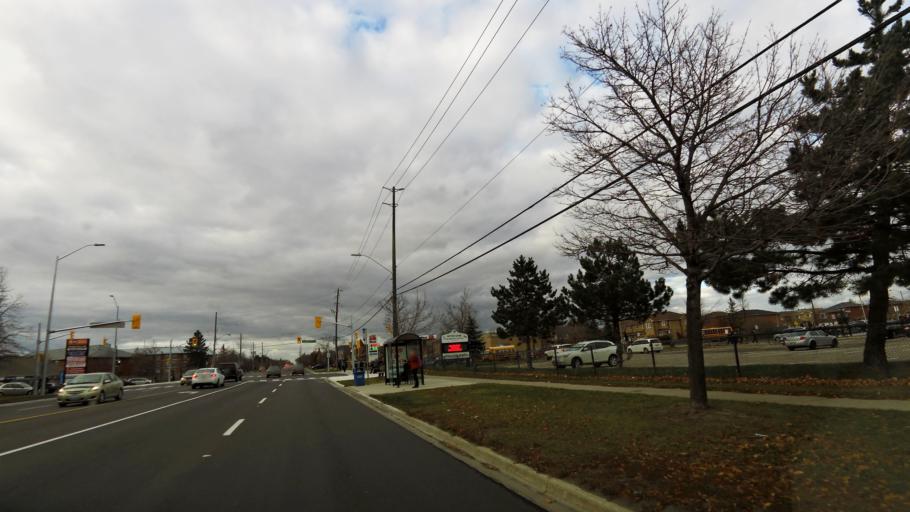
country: CA
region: Ontario
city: Brampton
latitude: 43.7189
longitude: -79.7806
